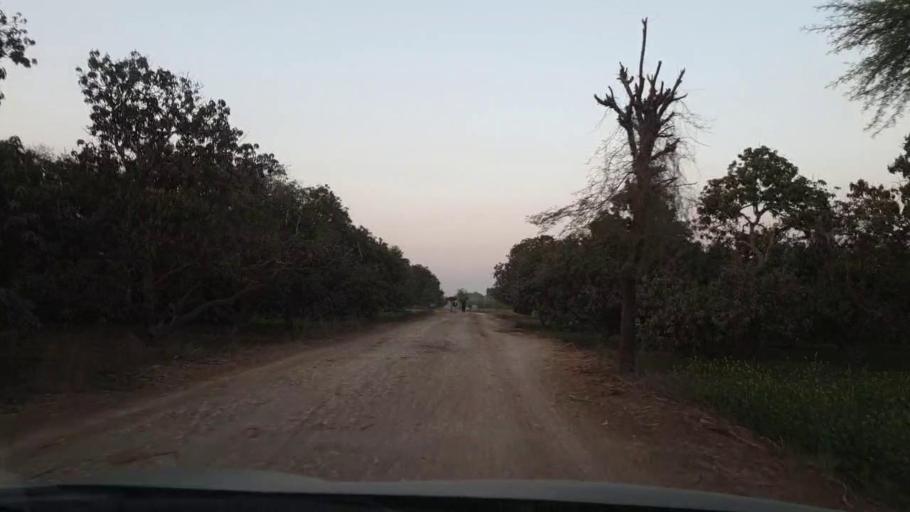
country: PK
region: Sindh
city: Berani
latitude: 25.6636
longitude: 68.7885
